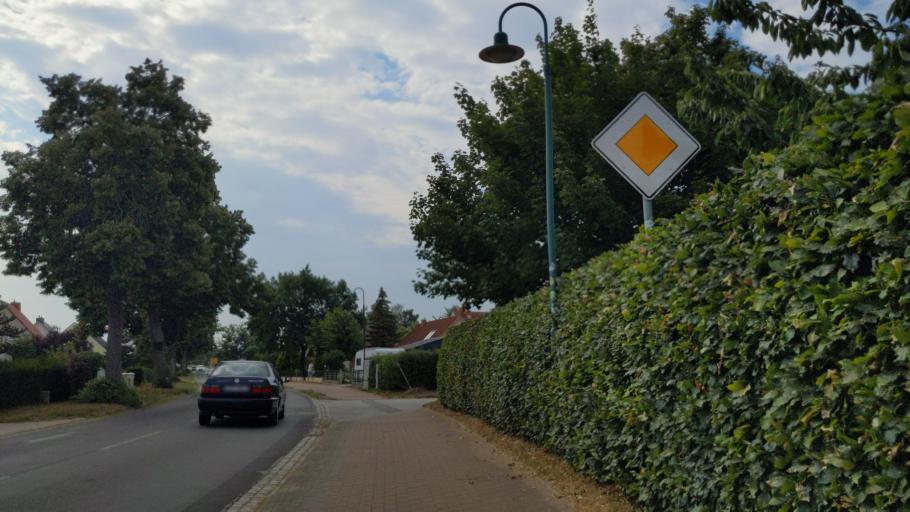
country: DE
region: Schleswig-Holstein
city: Gross Gronau
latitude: 53.8329
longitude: 10.8065
